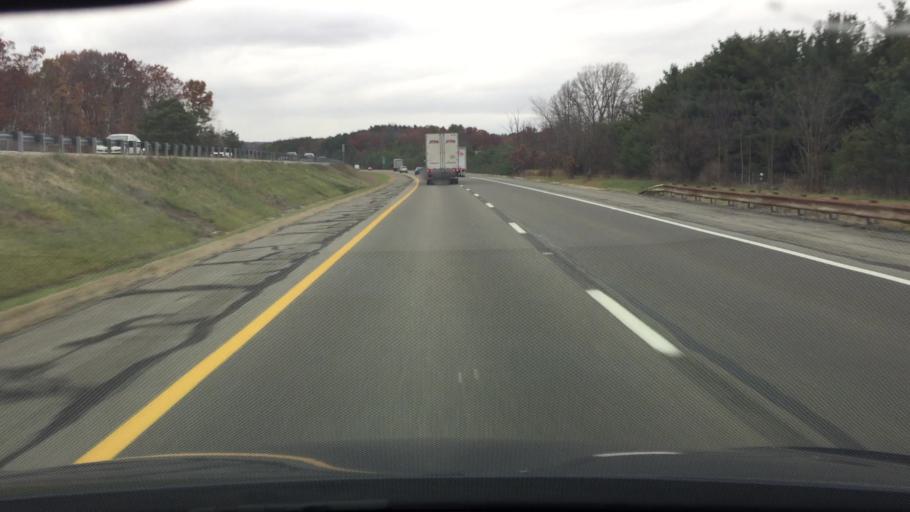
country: US
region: Ohio
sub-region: Mahoning County
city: Austintown
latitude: 41.0749
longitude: -80.7963
